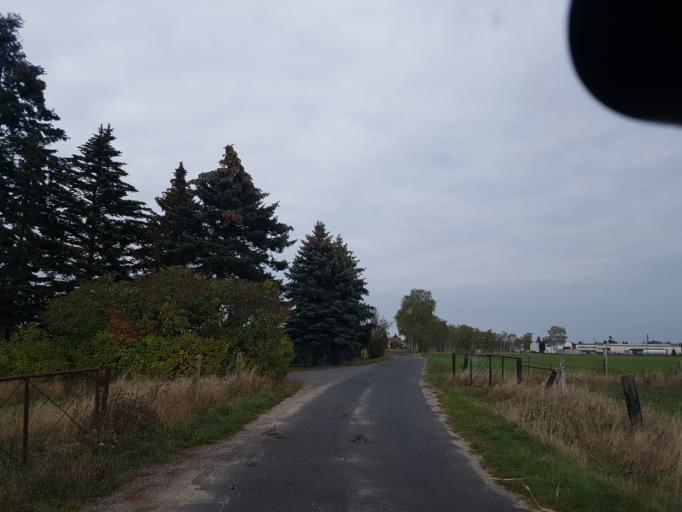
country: DE
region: Brandenburg
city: Finsterwalde
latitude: 51.6184
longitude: 13.6928
